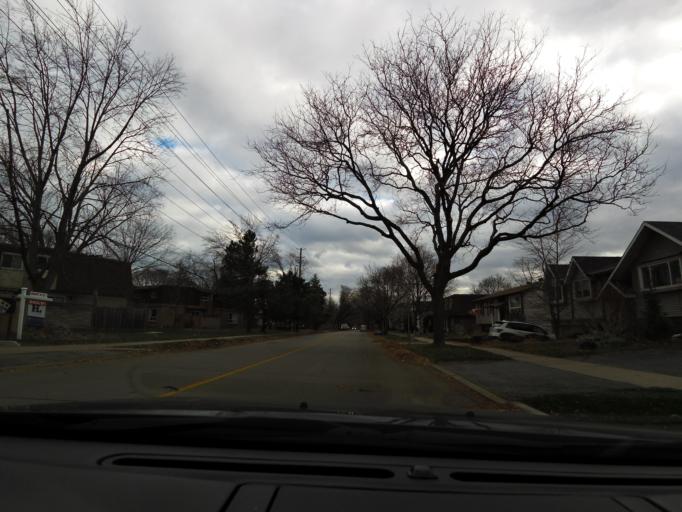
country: CA
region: Ontario
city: Burlington
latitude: 43.3165
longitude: -79.8166
